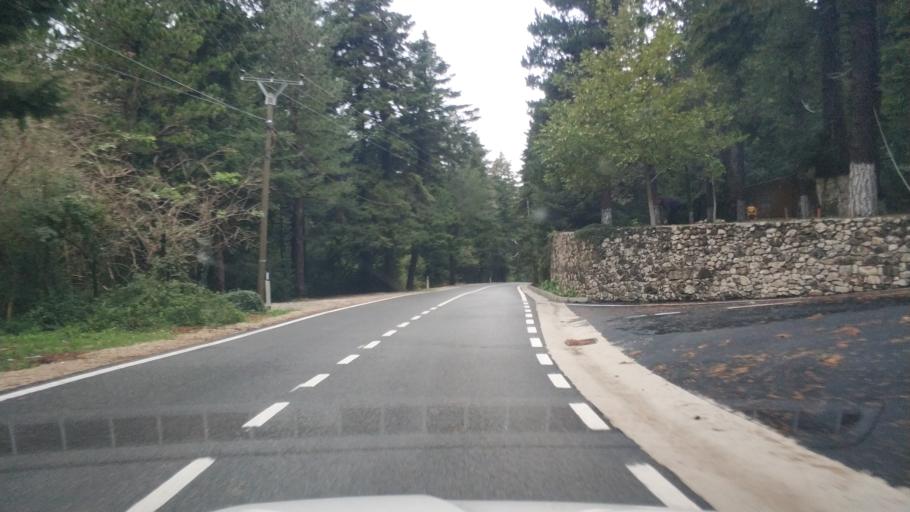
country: AL
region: Vlore
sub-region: Rrethi i Vlores
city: Brataj
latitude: 40.2080
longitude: 19.5810
